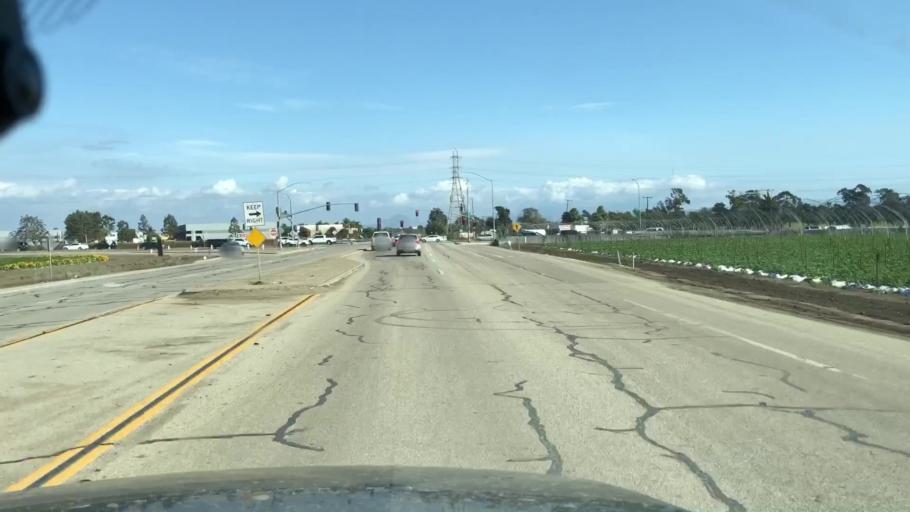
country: US
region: California
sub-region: Ventura County
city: El Rio
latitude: 34.2445
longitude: -119.2166
